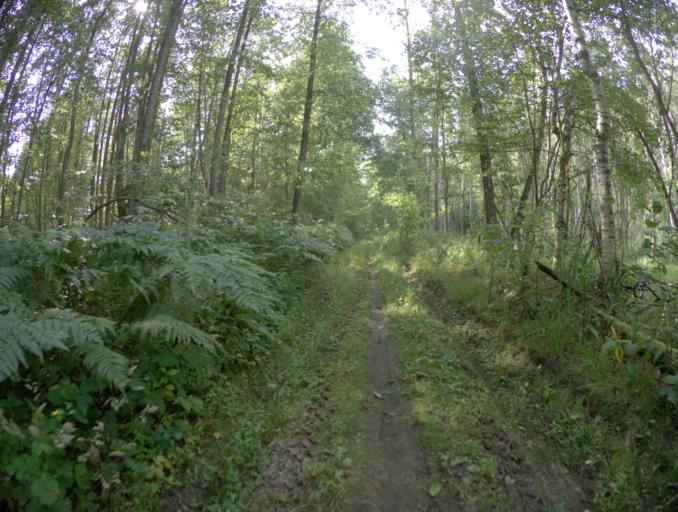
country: RU
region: Vladimir
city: Sobinka
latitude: 55.9100
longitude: 40.1207
